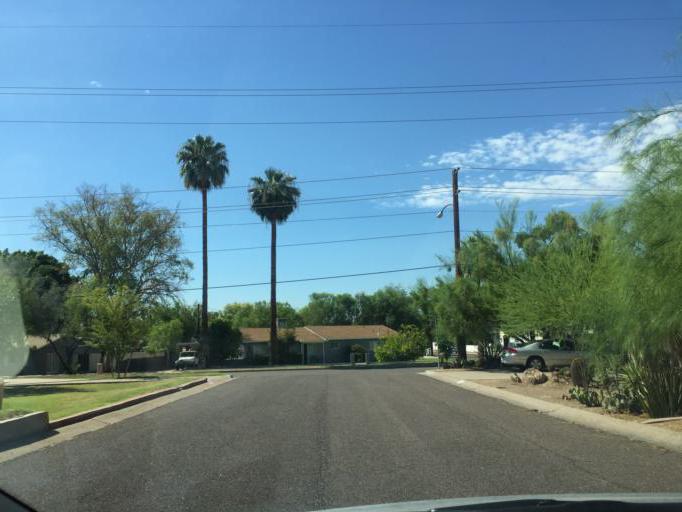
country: US
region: Arizona
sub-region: Maricopa County
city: Phoenix
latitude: 33.5350
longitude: -112.0502
